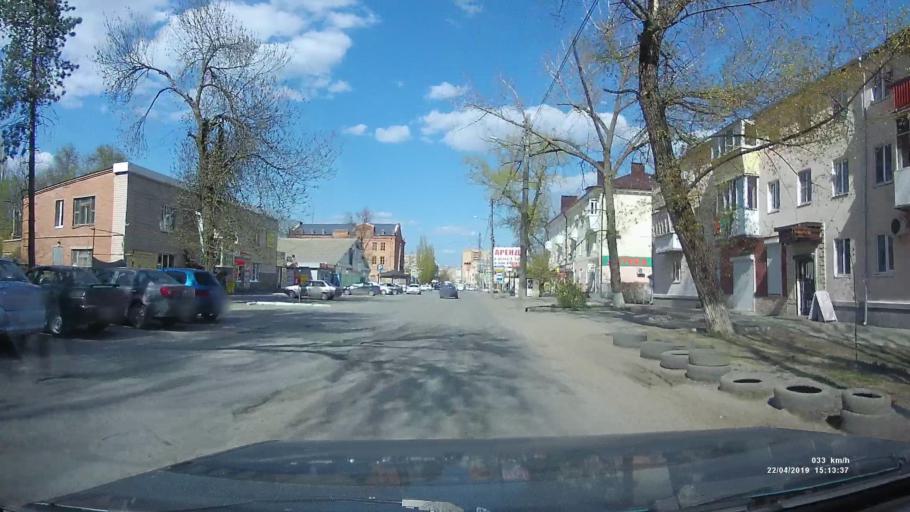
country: RU
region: Rostov
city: Azov
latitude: 47.1031
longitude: 39.4240
